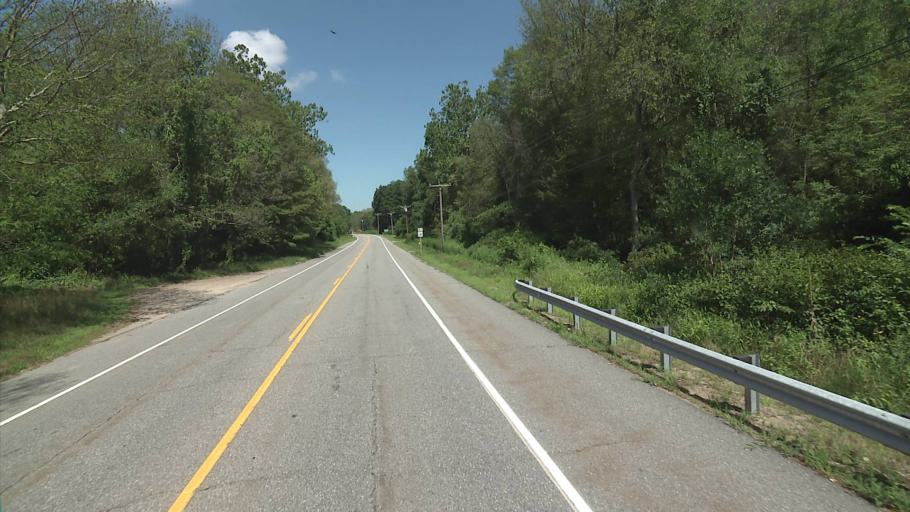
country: US
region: Connecticut
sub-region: Windham County
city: Plainfield Village
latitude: 41.6951
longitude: -71.9586
